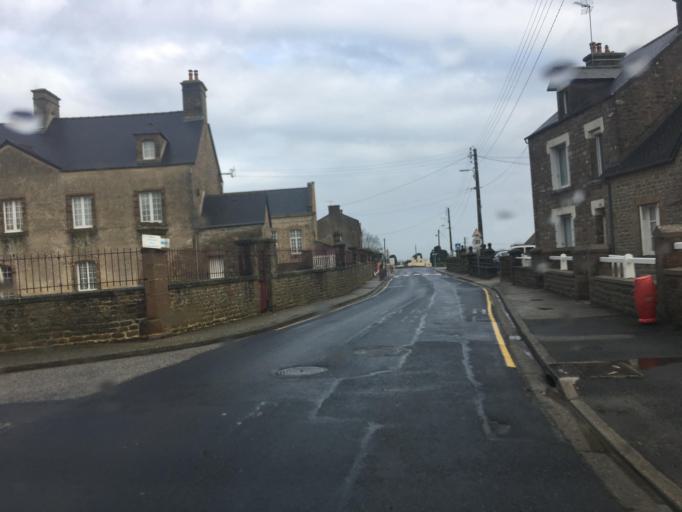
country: FR
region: Lower Normandy
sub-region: Departement de la Manche
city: Saint-Pierre-Eglise
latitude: 49.6702
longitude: -1.4052
